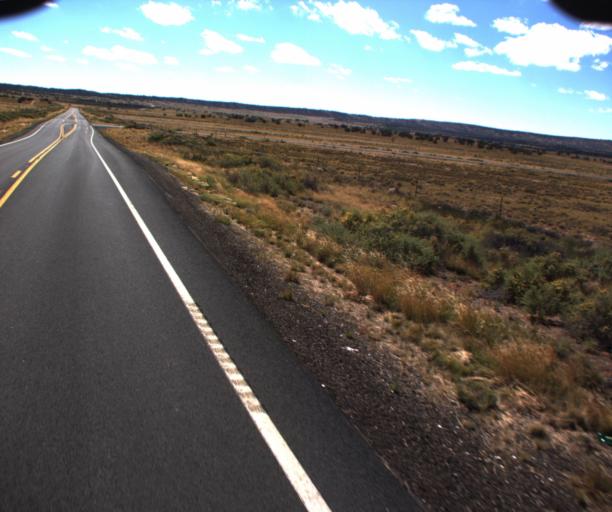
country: US
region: Arizona
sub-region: Apache County
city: Houck
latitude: 35.0650
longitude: -109.2831
